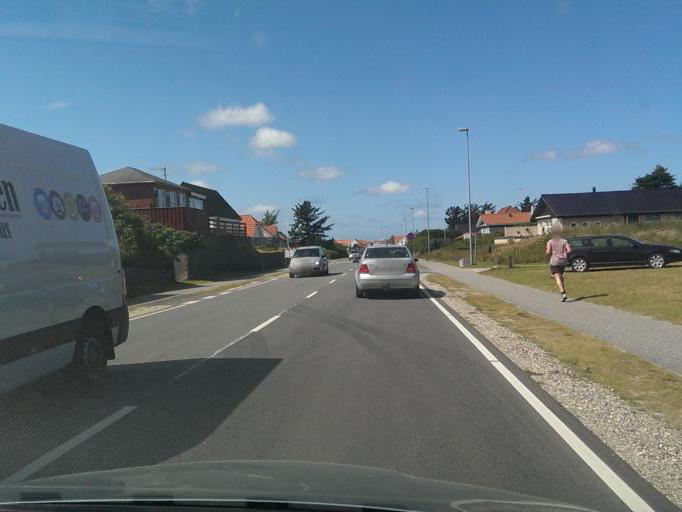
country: DK
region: North Denmark
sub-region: Jammerbugt Kommune
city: Pandrup
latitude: 57.2508
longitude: 9.5941
